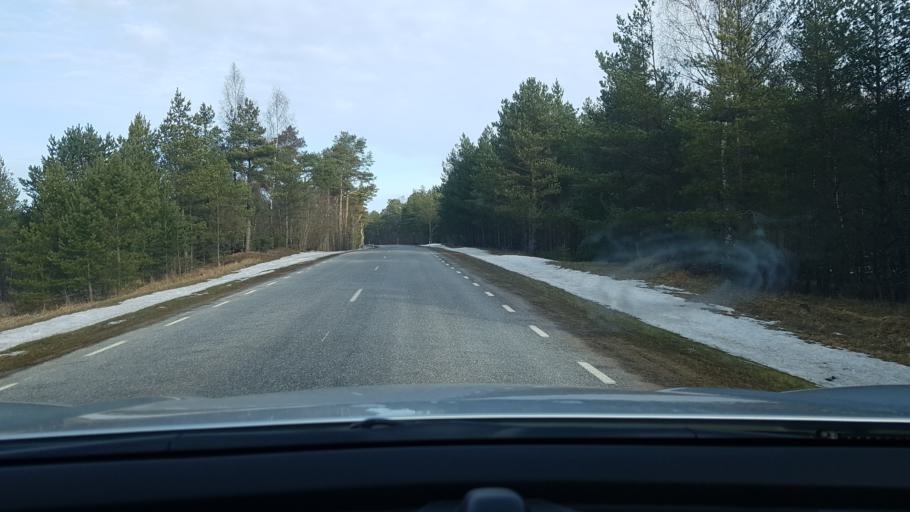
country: EE
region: Saare
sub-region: Kuressaare linn
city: Kuressaare
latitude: 58.4456
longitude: 22.7072
